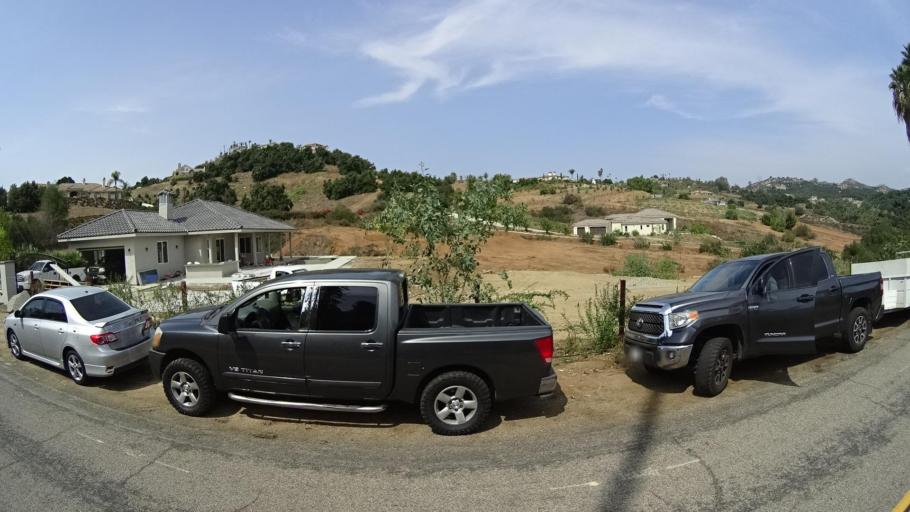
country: US
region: California
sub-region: San Diego County
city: Escondido
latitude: 33.0970
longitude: -117.0304
